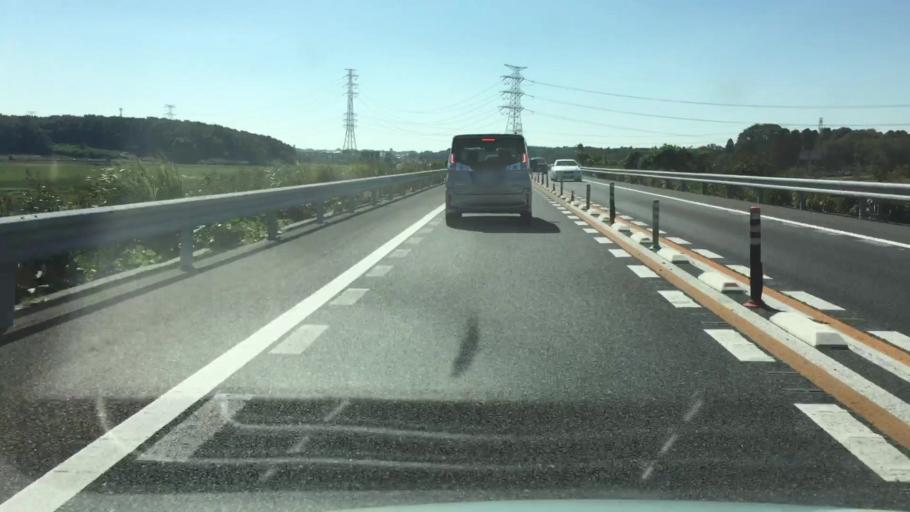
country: JP
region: Ibaraki
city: Ushiku
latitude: 36.0111
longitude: 140.1431
